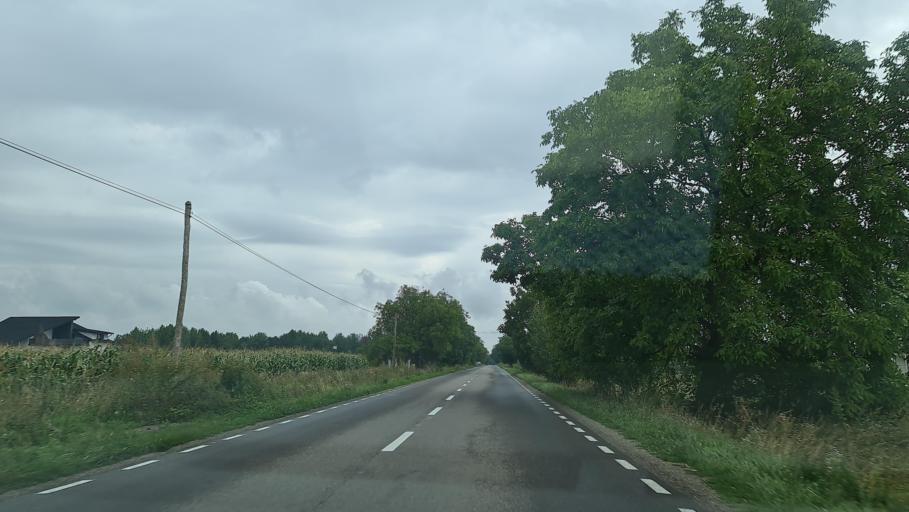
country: RO
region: Neamt
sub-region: Comuna Borlesti
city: Borlesti
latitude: 46.7666
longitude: 26.4775
